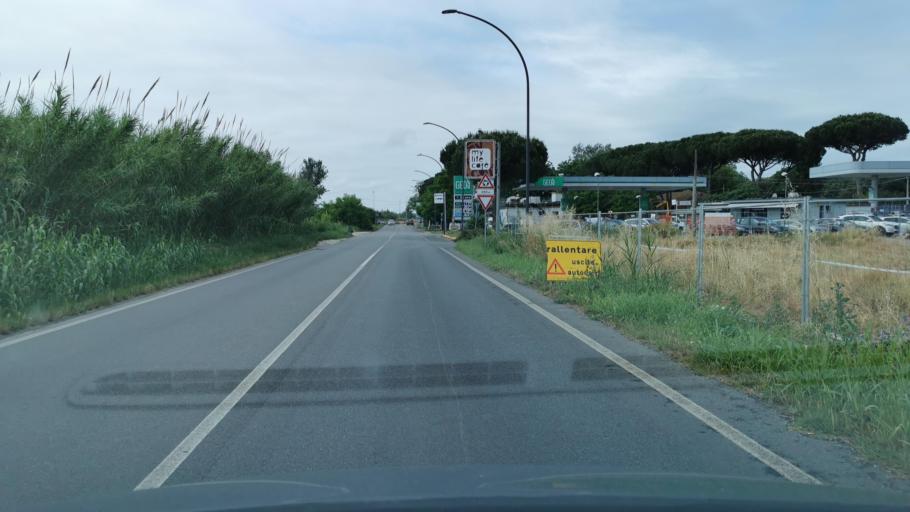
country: IT
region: Emilia-Romagna
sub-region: Provincia di Ravenna
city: Madonna Dell'Albero
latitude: 44.3874
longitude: 12.1962
